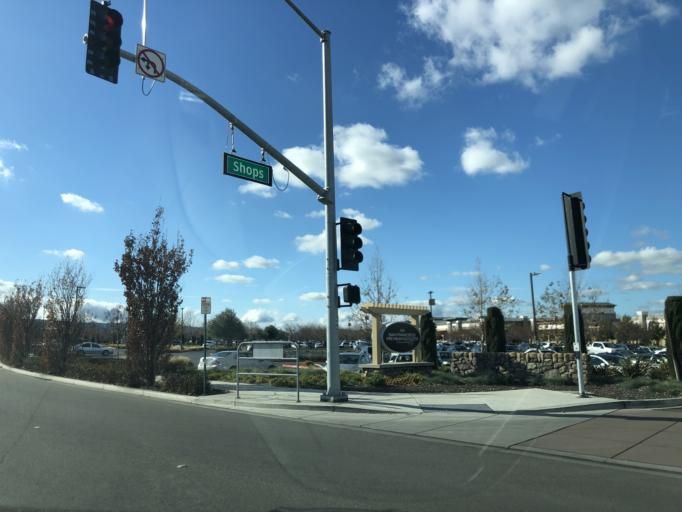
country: US
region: California
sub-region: Alameda County
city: Pleasanton
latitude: 37.6976
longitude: -121.8407
